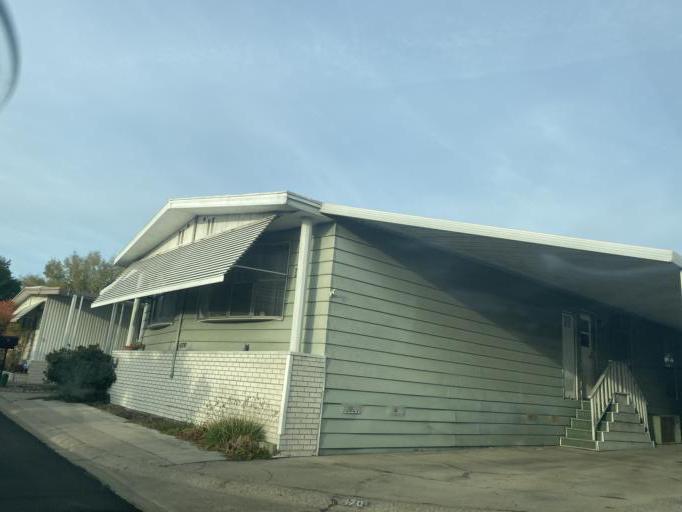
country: US
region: California
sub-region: Orange County
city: Brea
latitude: 33.9069
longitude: -117.8787
